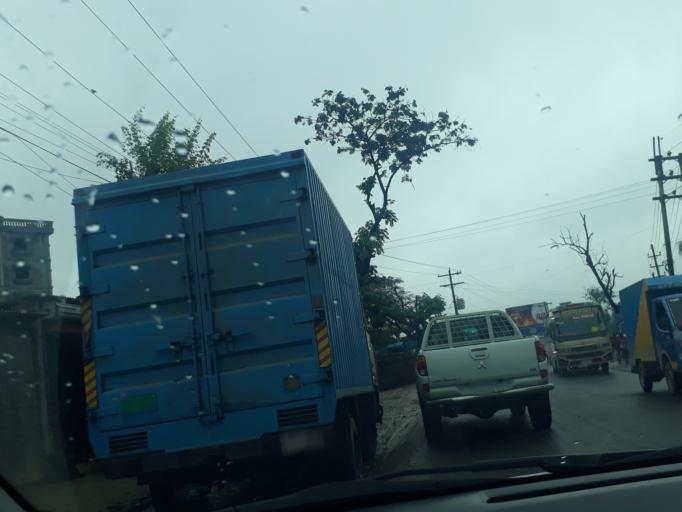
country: BD
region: Dhaka
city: Tungi
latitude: 23.9029
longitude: 90.3257
